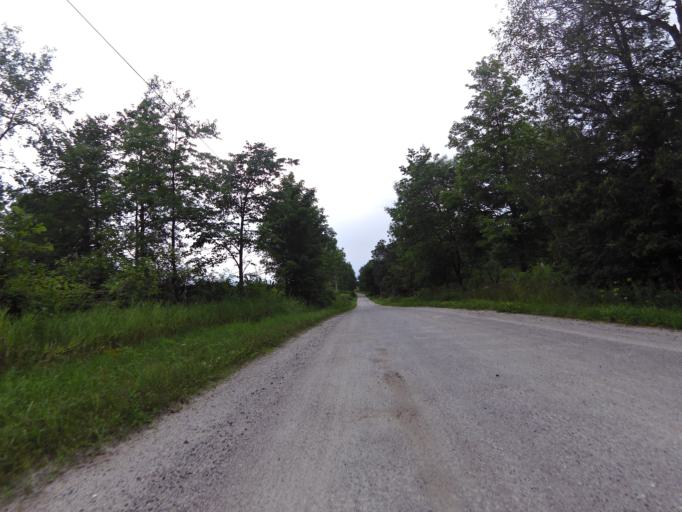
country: CA
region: Ontario
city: Perth
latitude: 44.8601
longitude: -76.5600
